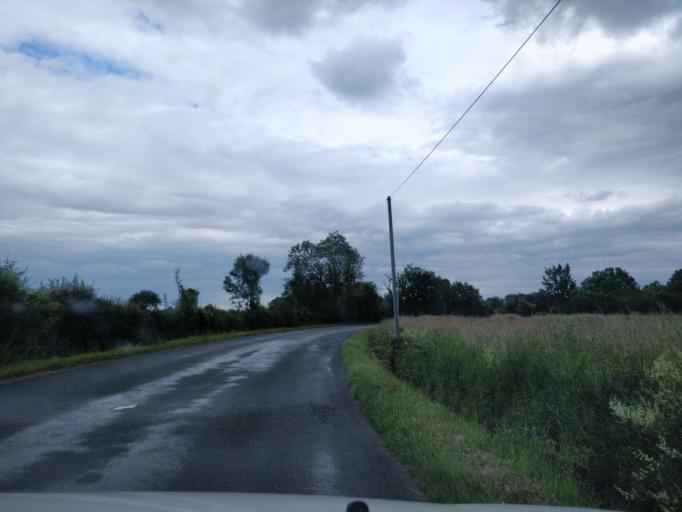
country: FR
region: Pays de la Loire
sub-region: Departement de Maine-et-Loire
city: Grez-Neuville
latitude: 47.6373
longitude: -0.6361
